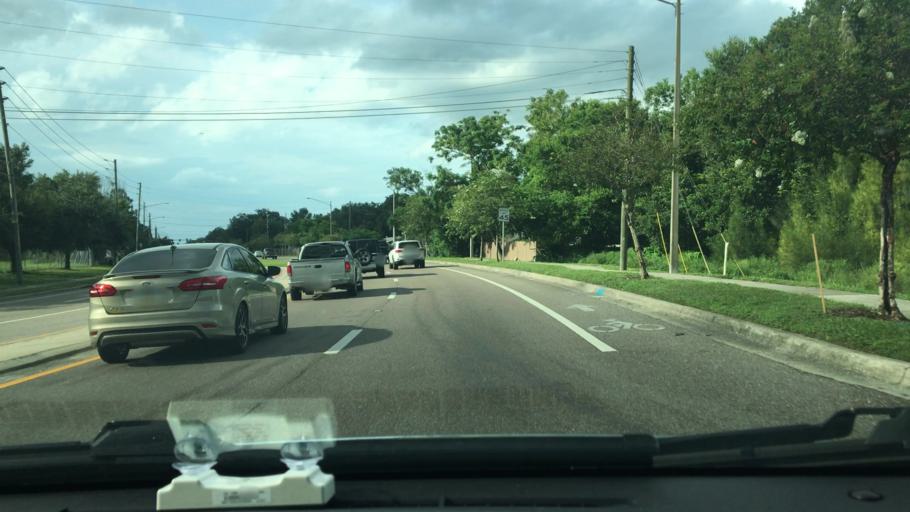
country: US
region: Florida
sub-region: Orange County
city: Azalea Park
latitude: 28.5225
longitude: -81.2862
